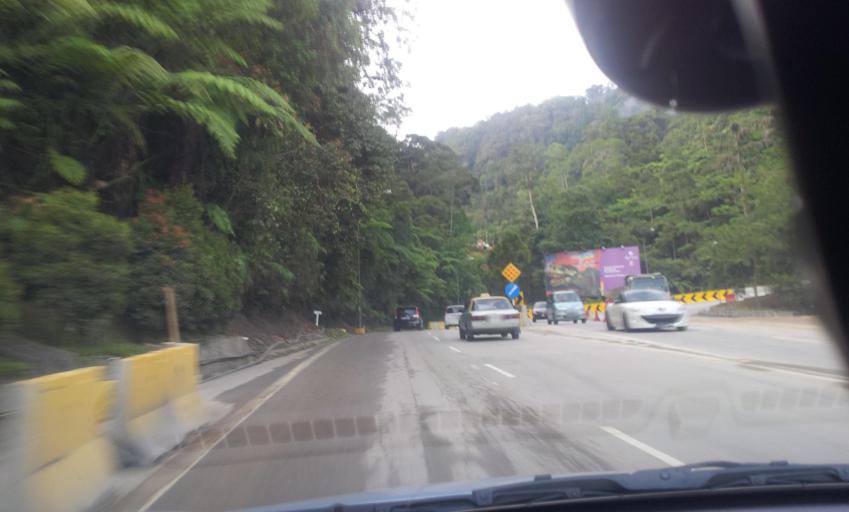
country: MY
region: Pahang
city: Kampung Bukit Tinggi, Bentong
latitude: 3.4030
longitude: 101.7850
